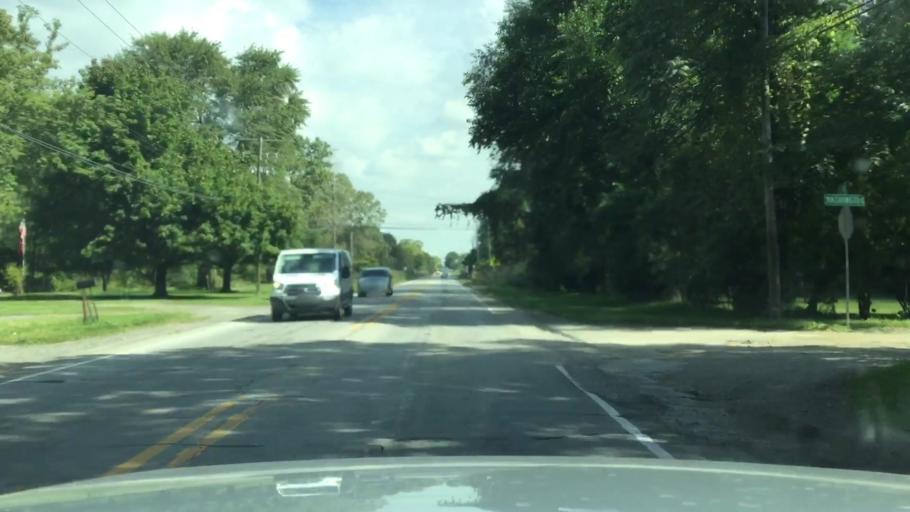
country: US
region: Michigan
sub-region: Wayne County
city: Wayne
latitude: 42.2520
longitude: -83.3842
